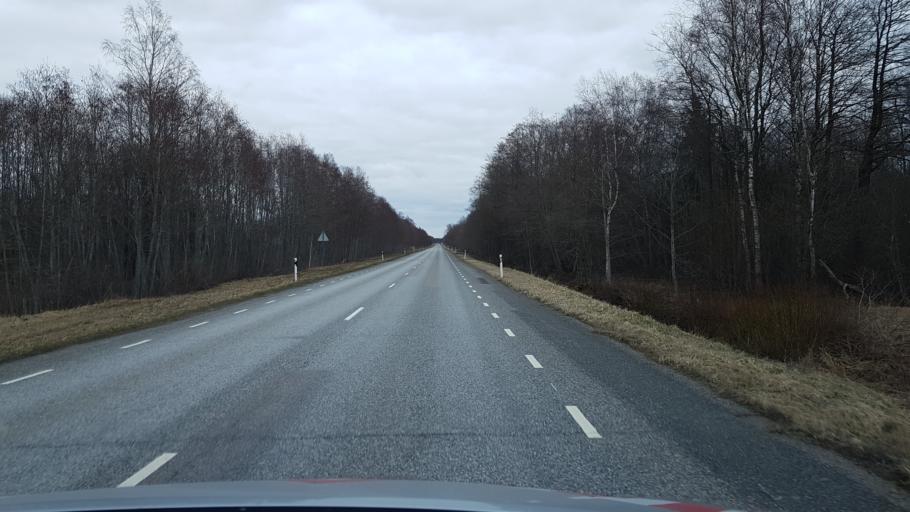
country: EE
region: Ida-Virumaa
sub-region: Narva-Joesuu linn
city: Narva-Joesuu
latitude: 59.3449
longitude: 28.0044
